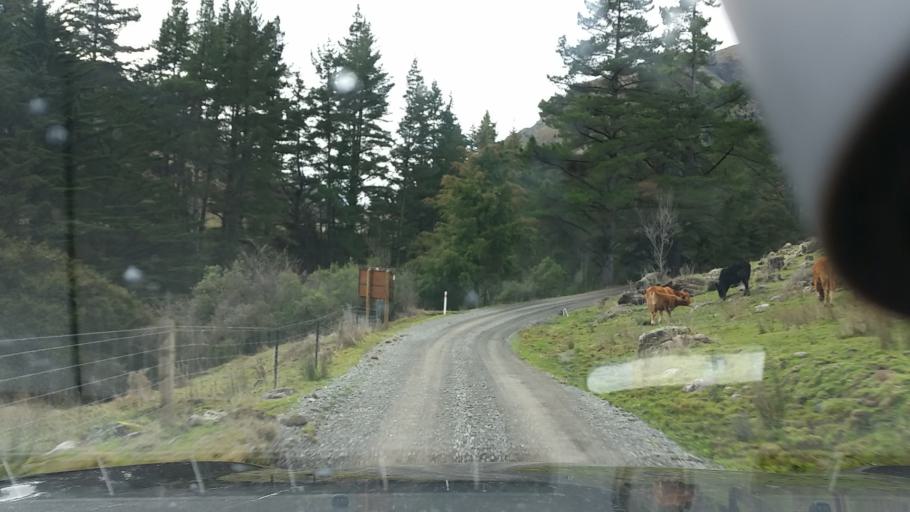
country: NZ
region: Tasman
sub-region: Tasman District
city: Richmond
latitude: -41.7308
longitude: 173.4659
